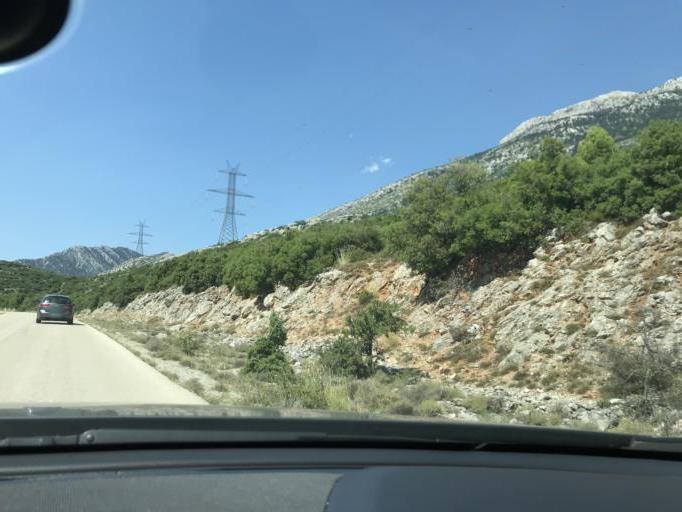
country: GR
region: Central Greece
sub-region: Nomos Voiotias
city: Distomo
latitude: 38.4978
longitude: 22.7000
